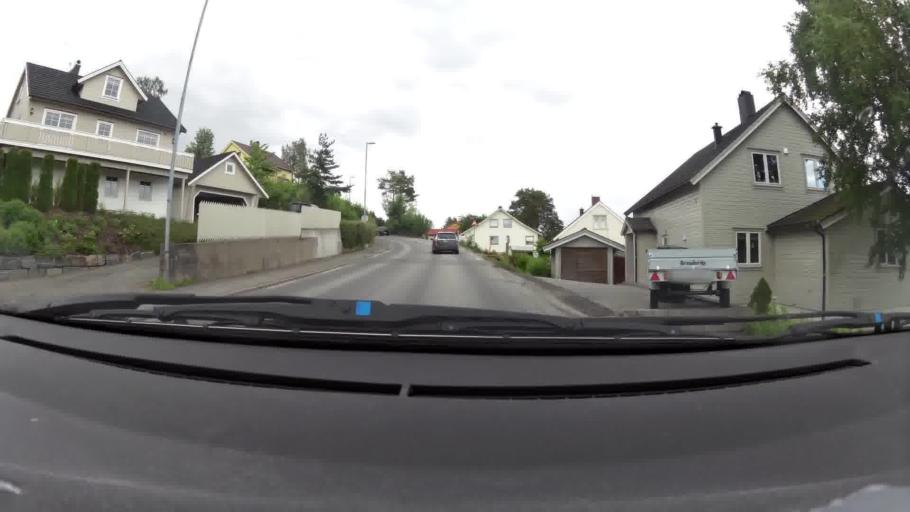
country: NO
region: More og Romsdal
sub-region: Molde
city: Molde
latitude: 62.7455
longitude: 7.2326
